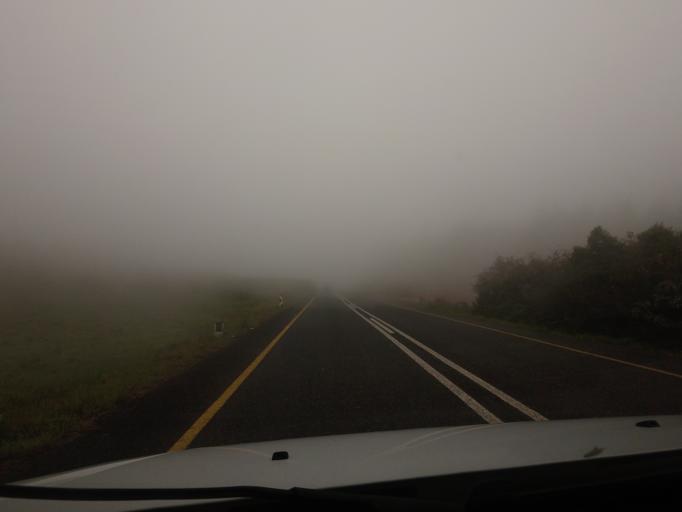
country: ZA
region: Mpumalanga
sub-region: Ehlanzeni District
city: Lydenburg
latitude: -25.1634
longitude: 30.6345
